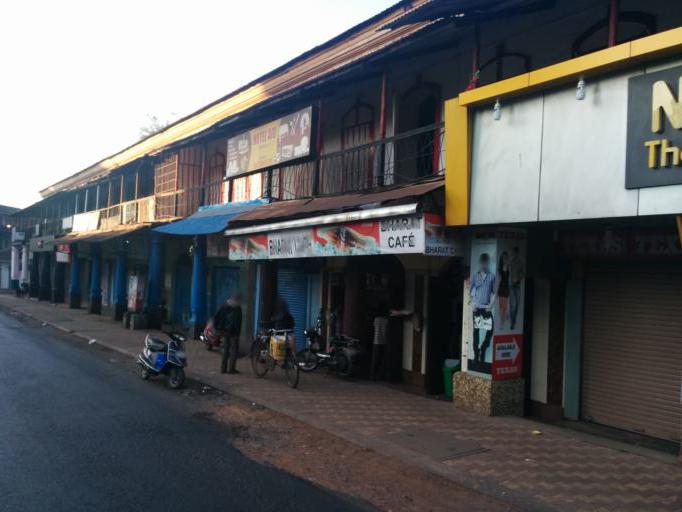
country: IN
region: Goa
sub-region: South Goa
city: Madgaon
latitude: 15.2711
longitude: 73.9589
